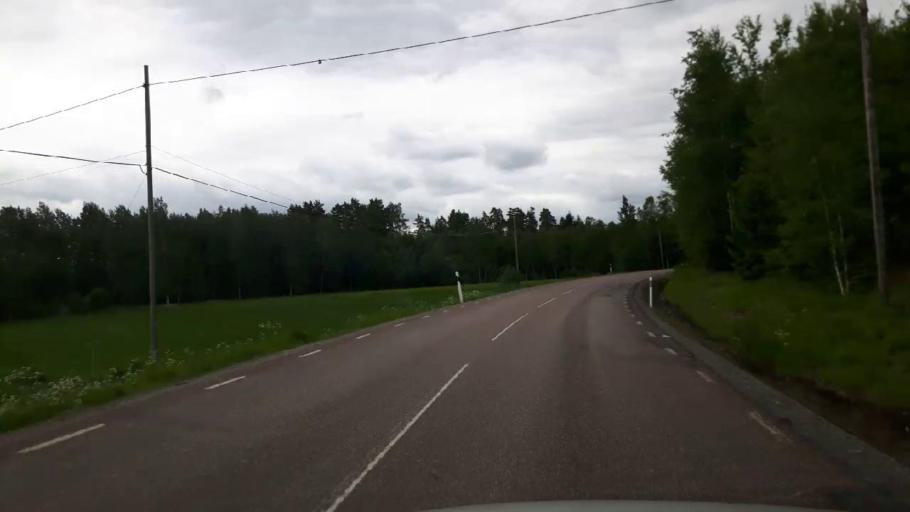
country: SE
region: Vaestmanland
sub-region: Kopings Kommun
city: Kolsva
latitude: 59.7111
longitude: 15.7985
